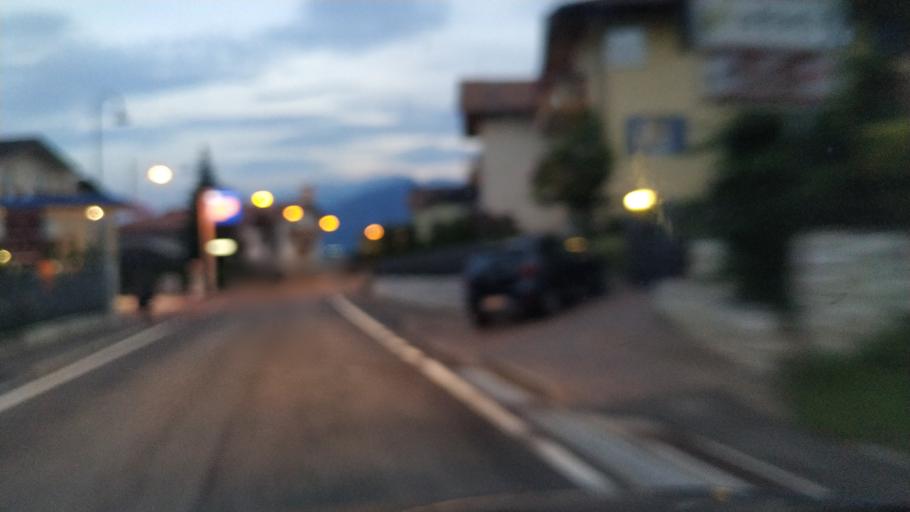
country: IT
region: Trentino-Alto Adige
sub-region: Provincia di Trento
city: Romallo
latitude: 46.3936
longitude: 11.0632
